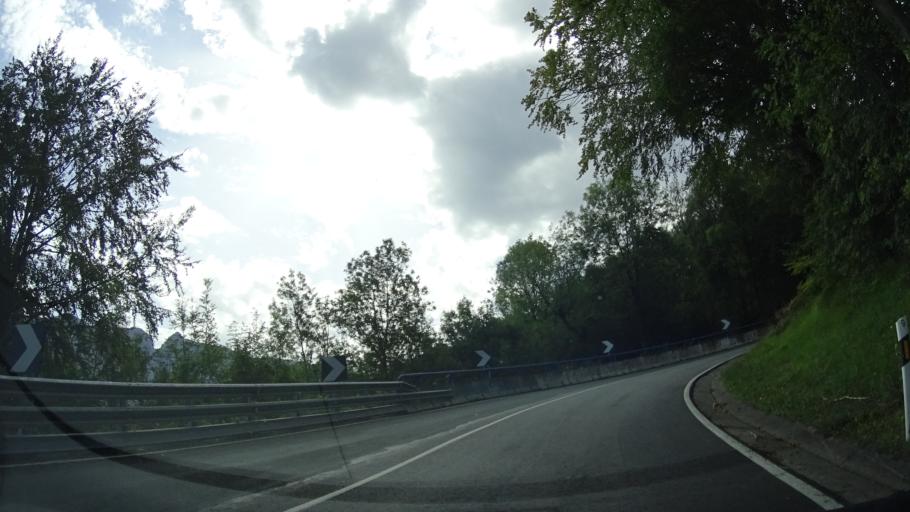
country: ES
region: Basque Country
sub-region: Bizkaia
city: Manaria
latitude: 43.1066
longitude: -2.6446
